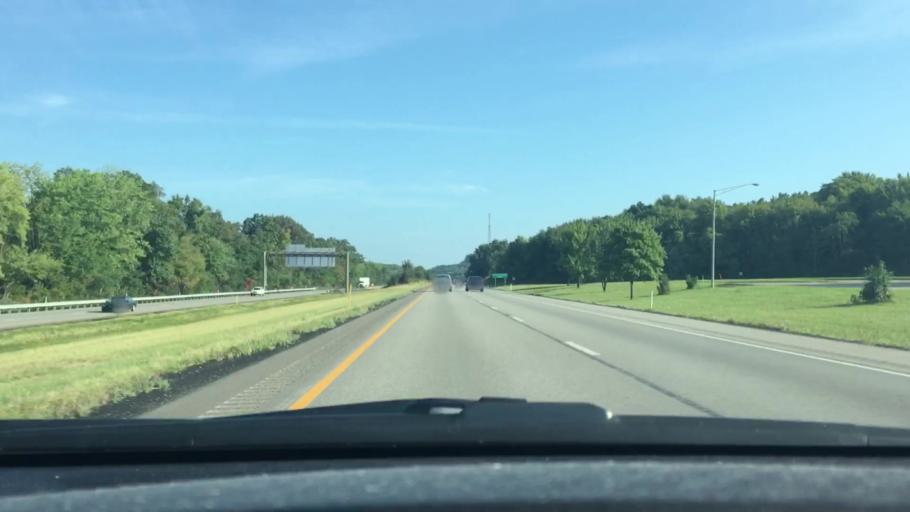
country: US
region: Pennsylvania
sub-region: Butler County
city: Fox Run
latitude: 40.7097
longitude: -80.1017
